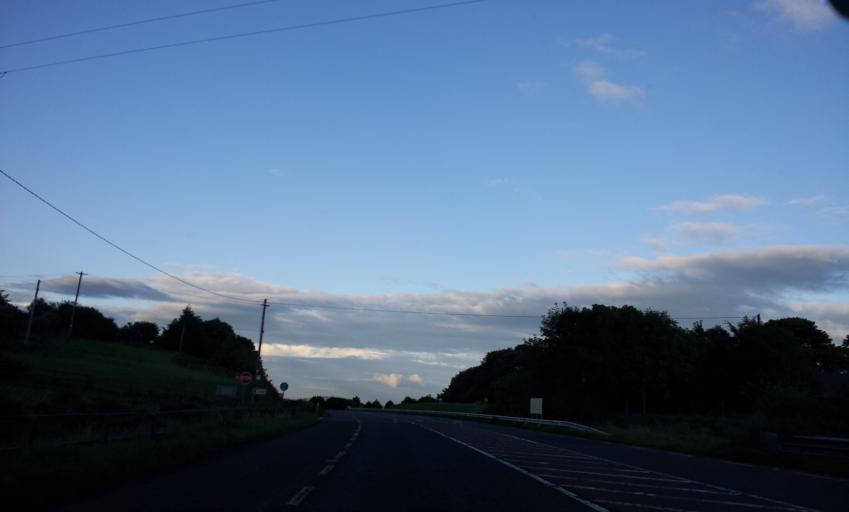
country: IE
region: Munster
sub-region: County Limerick
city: Newcastle West
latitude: 52.4202
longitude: -9.1375
